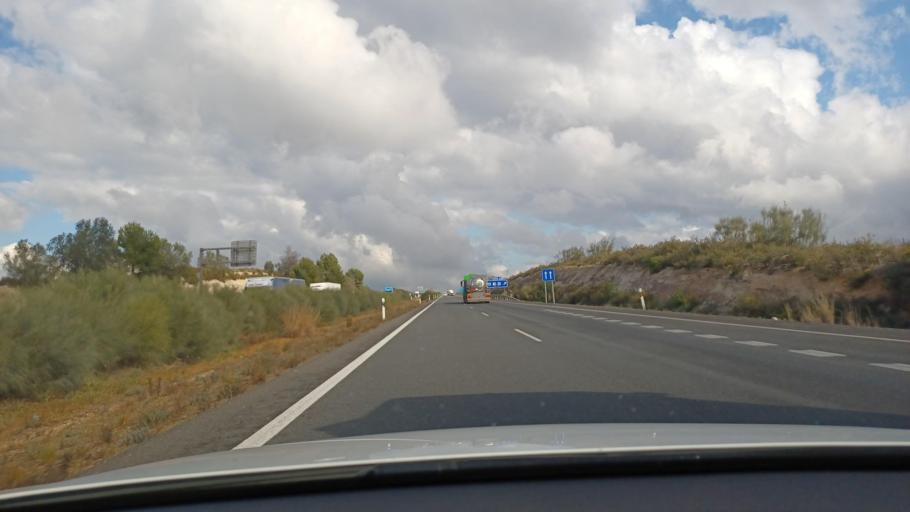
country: ES
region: Valencia
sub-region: Provincia de Valencia
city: Vallada
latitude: 38.9183
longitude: -0.6812
